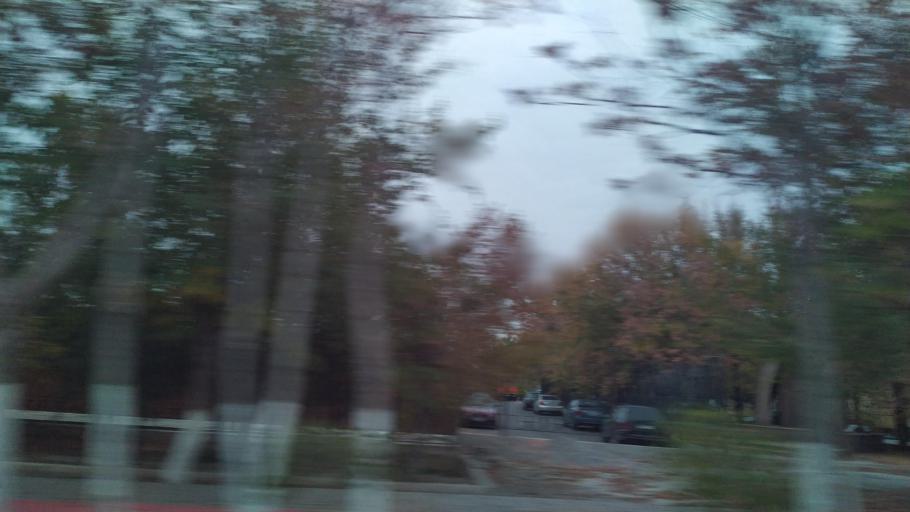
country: KZ
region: Ongtustik Qazaqstan
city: Turkestan
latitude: 43.2987
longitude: 68.2776
